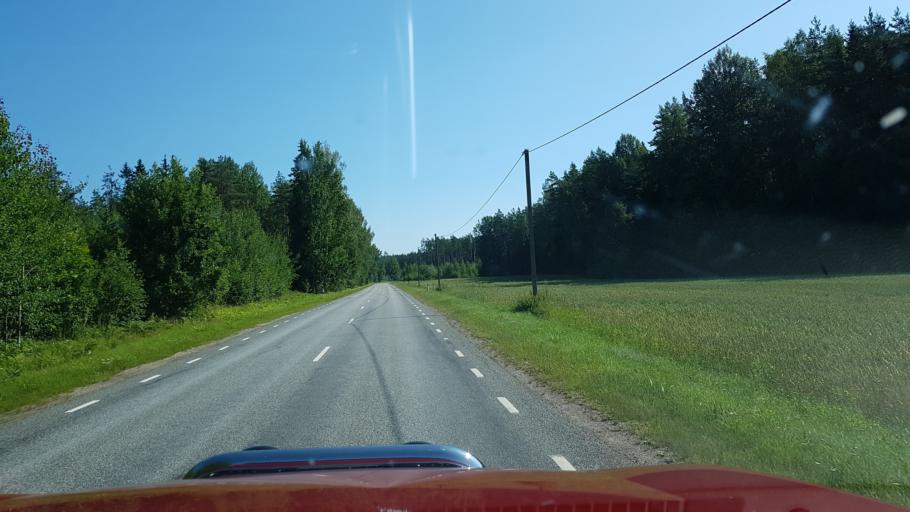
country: EE
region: Polvamaa
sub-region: Polva linn
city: Polva
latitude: 58.0039
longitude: 26.9378
